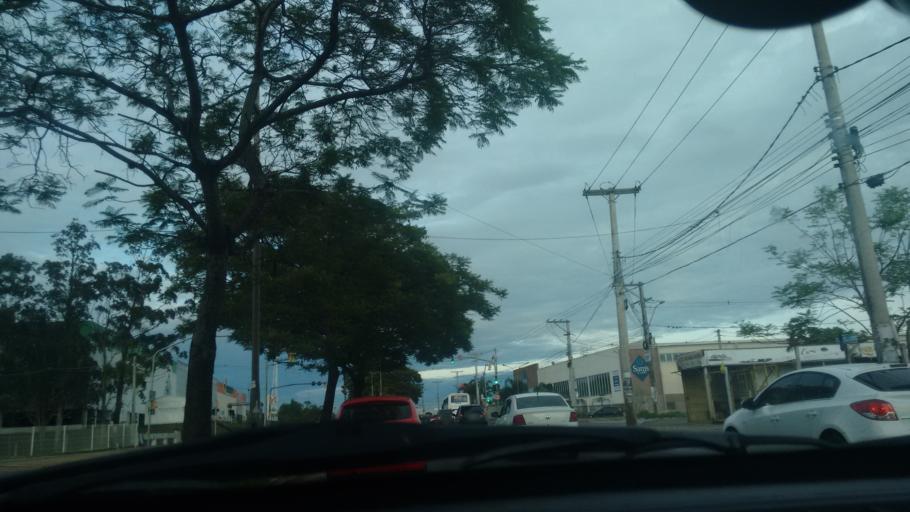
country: BR
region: Rio Grande do Sul
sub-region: Cachoeirinha
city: Cachoeirinha
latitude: -29.9979
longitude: -51.1390
